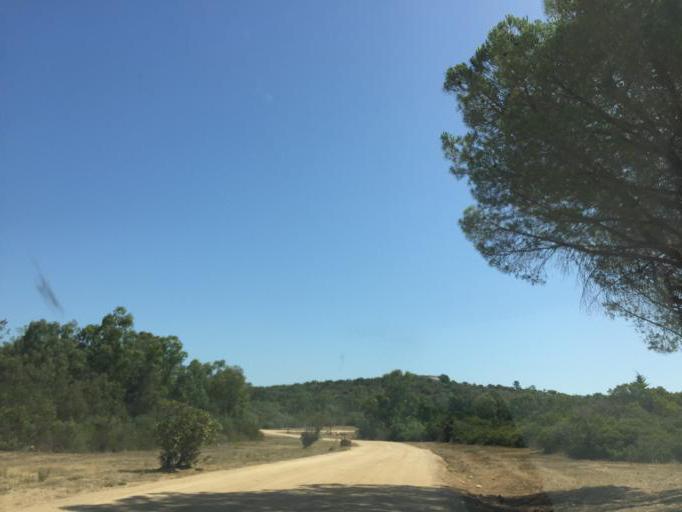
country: IT
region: Sardinia
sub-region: Provincia di Olbia-Tempio
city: San Teodoro
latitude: 40.8358
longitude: 9.6805
